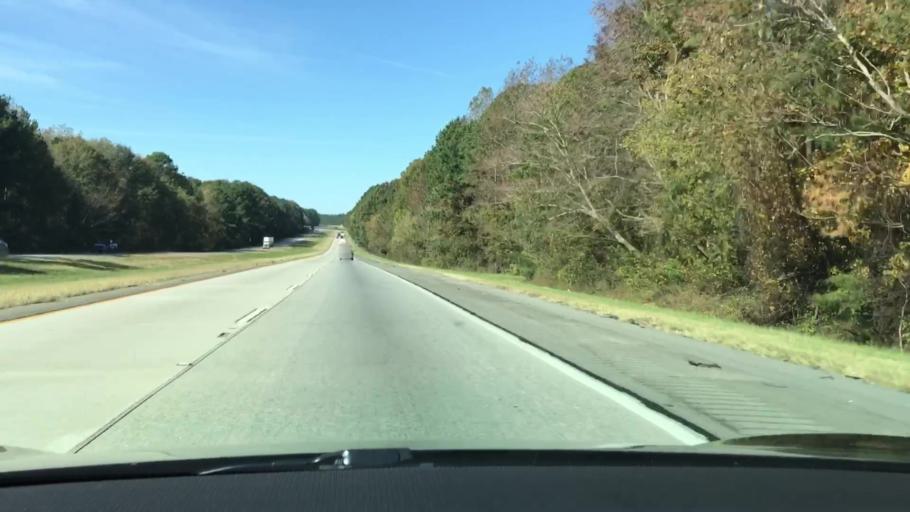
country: US
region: Georgia
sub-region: Greene County
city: Union Point
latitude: 33.5473
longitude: -83.0360
